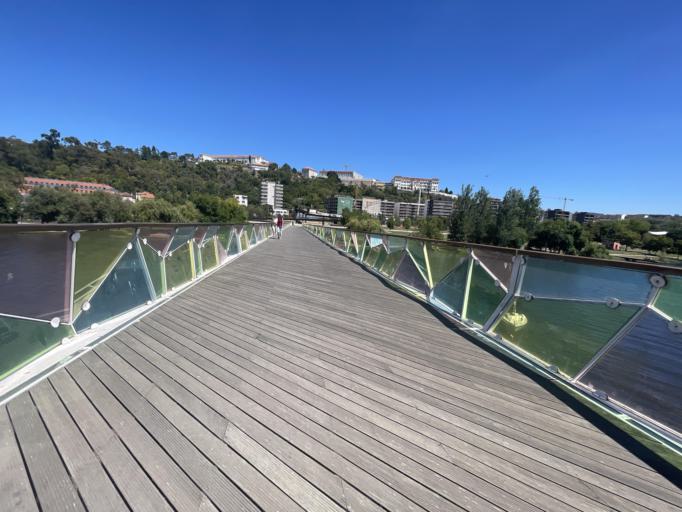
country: PT
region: Coimbra
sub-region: Coimbra
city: Coimbra
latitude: 40.2013
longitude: -8.4267
